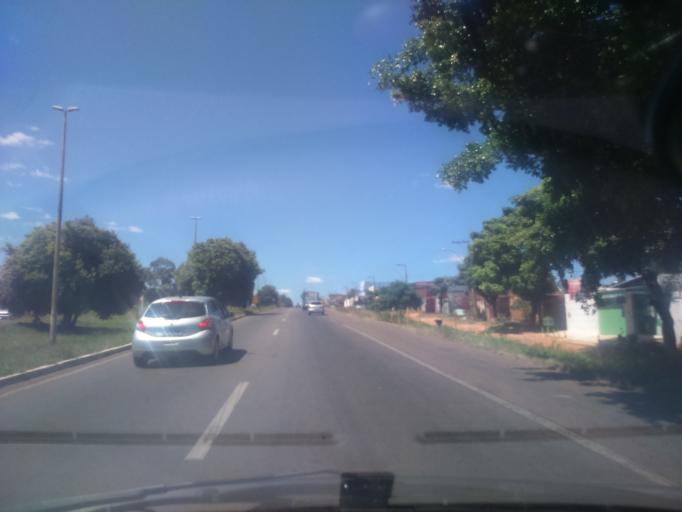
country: BR
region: Goias
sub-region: Luziania
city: Luziania
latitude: -16.0492
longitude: -48.0100
